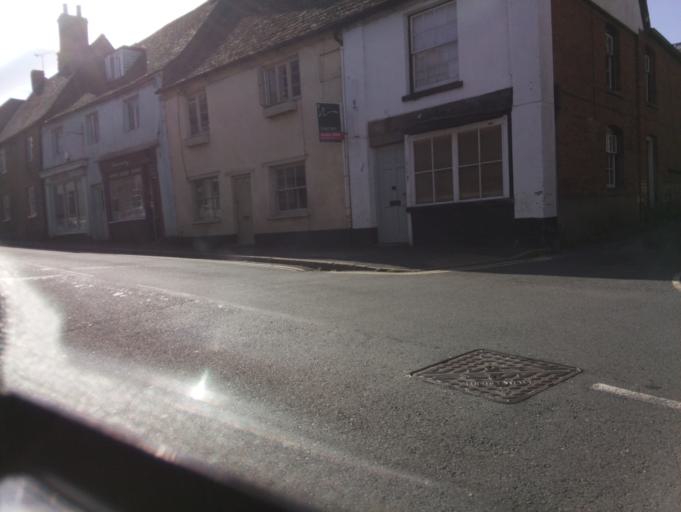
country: GB
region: England
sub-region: Oxfordshire
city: Faringdon
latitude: 51.6579
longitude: -1.5821
